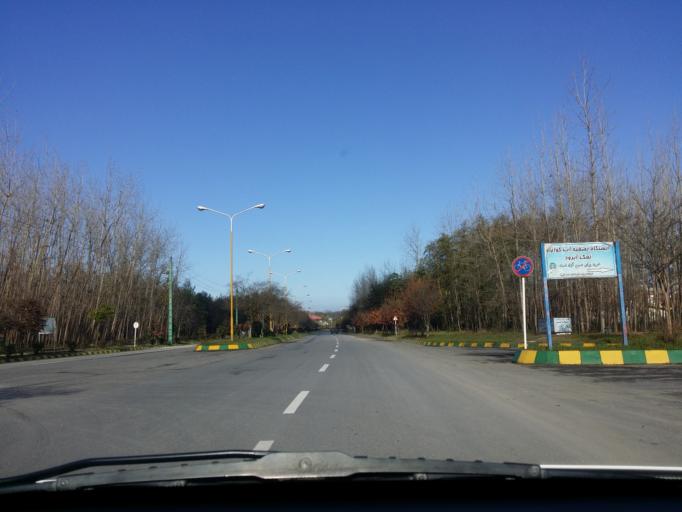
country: IR
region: Mazandaran
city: Chalus
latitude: 36.6783
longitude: 51.3065
